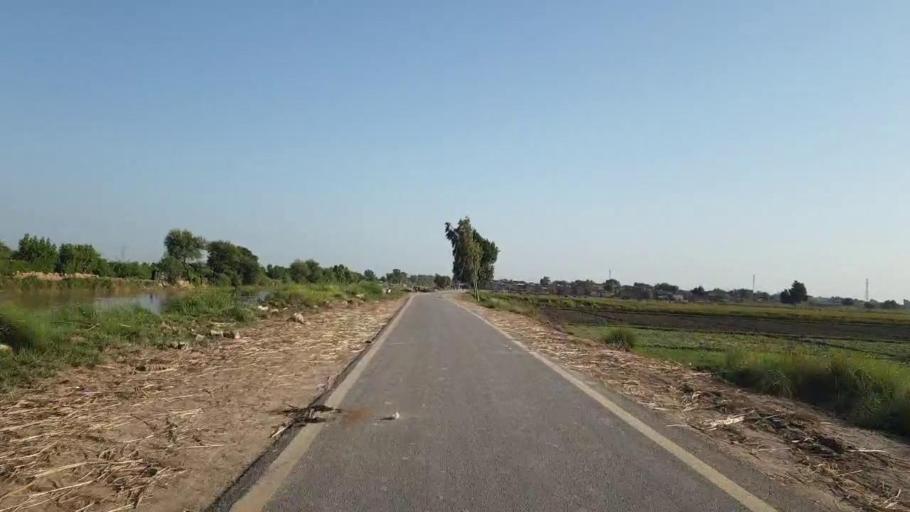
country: PK
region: Sindh
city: Hyderabad
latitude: 25.3268
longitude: 68.4254
